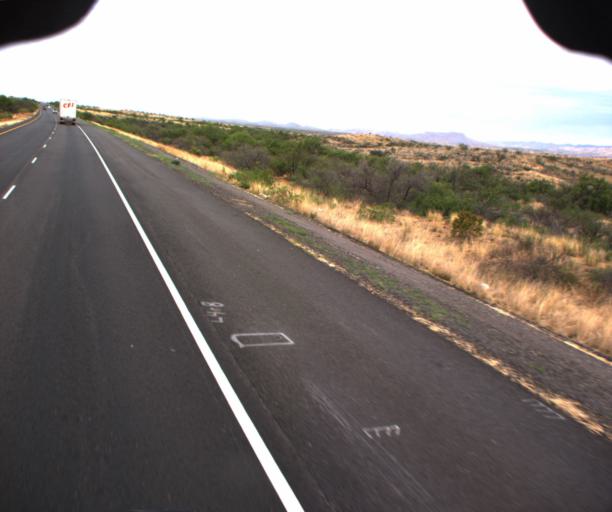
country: US
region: Arizona
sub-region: Cochise County
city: Mescal
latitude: 31.9718
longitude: -110.4802
